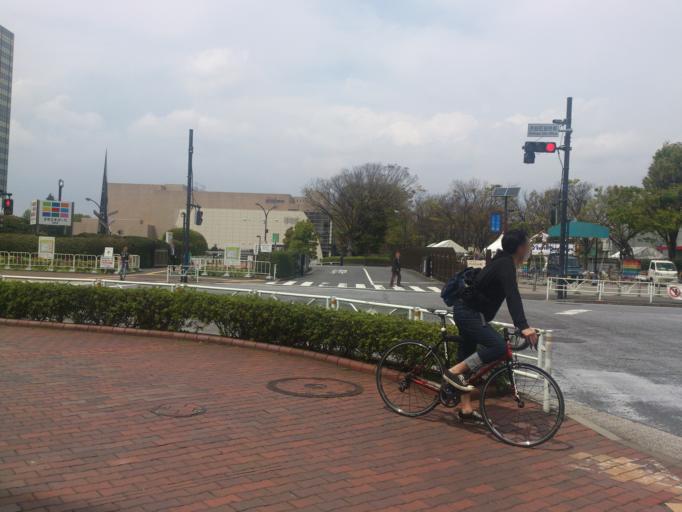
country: JP
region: Tokyo
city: Tokyo
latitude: 35.6645
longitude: 139.6989
